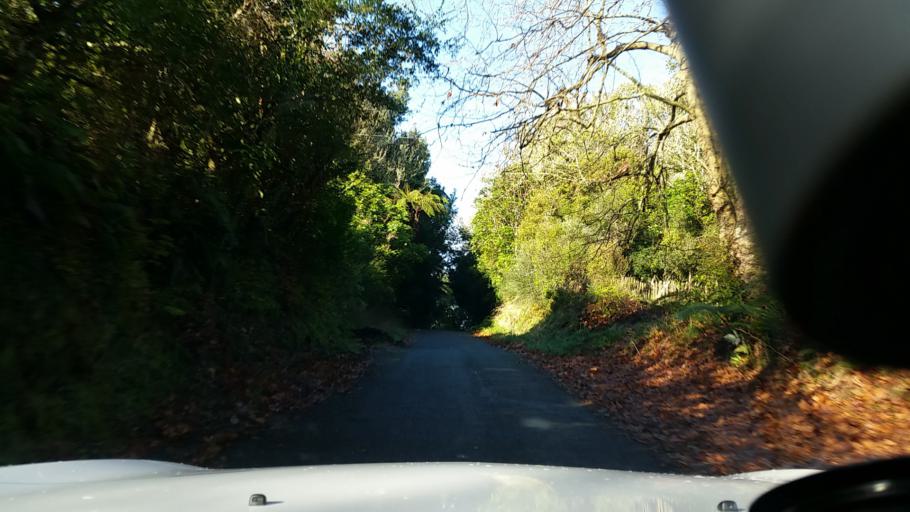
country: NZ
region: Bay of Plenty
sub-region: Kawerau District
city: Kawerau
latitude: -38.0181
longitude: 176.5780
